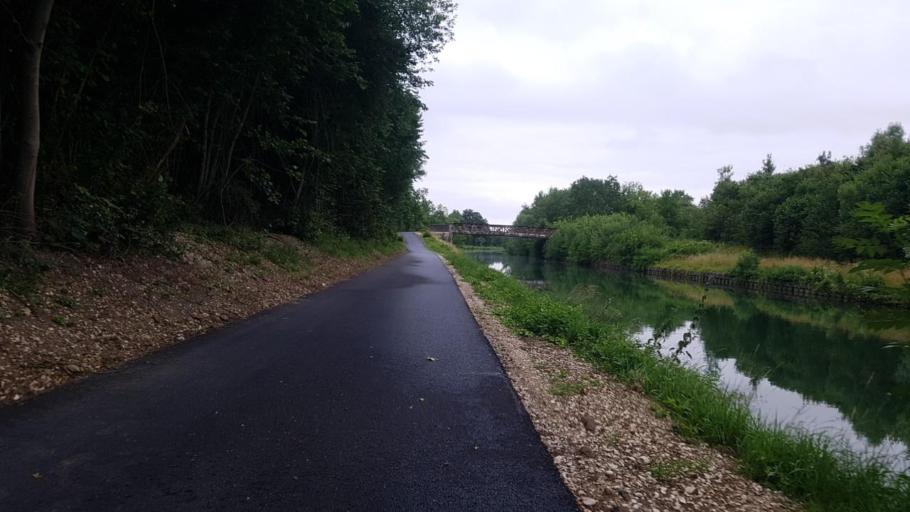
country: FR
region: Champagne-Ardenne
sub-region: Departement de la Marne
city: Vitry-le-Francois
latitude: 48.8252
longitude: 4.5155
